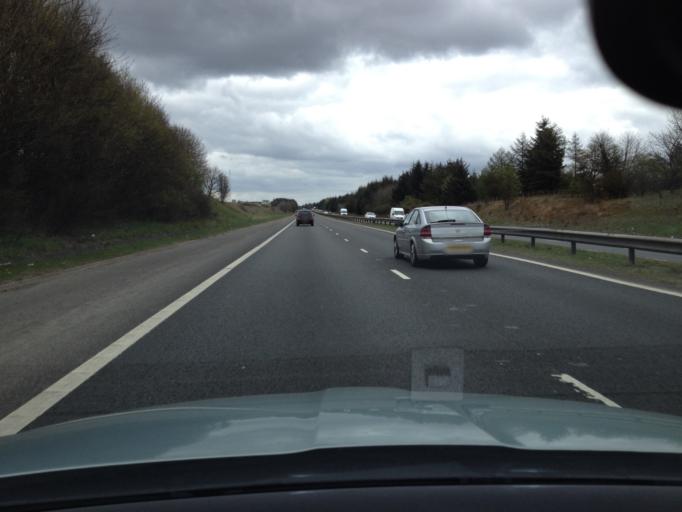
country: GB
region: Scotland
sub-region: North Lanarkshire
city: Caldercruix
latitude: 55.8457
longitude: -3.8769
